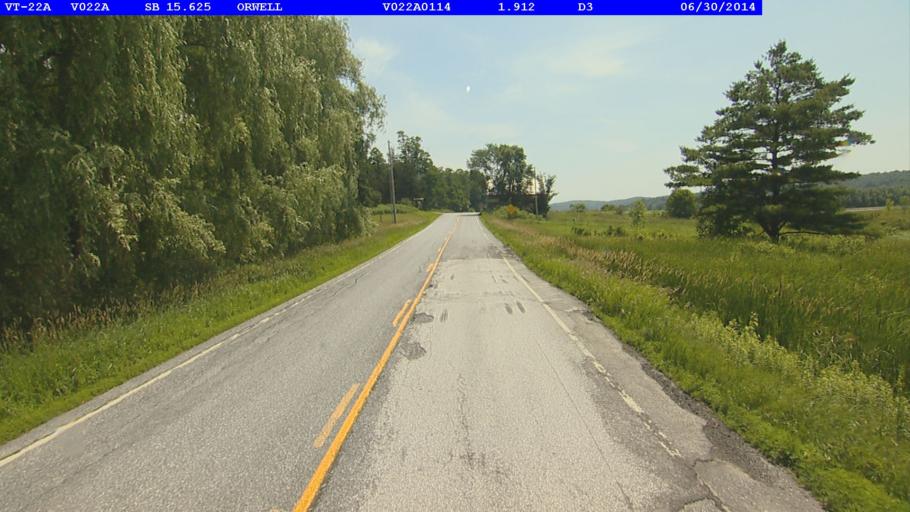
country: US
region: New York
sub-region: Essex County
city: Ticonderoga
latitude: 43.7845
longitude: -73.3068
